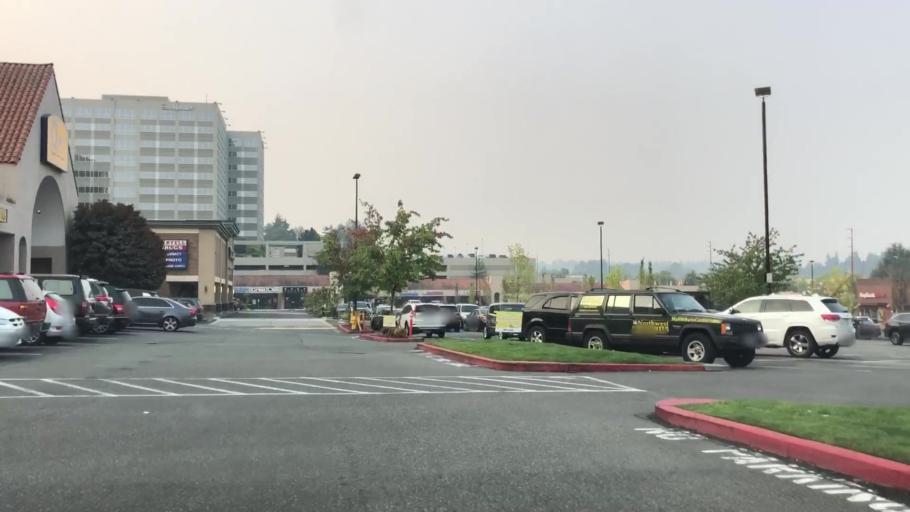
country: US
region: Washington
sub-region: King County
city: Newport
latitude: 47.5790
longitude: -122.1676
